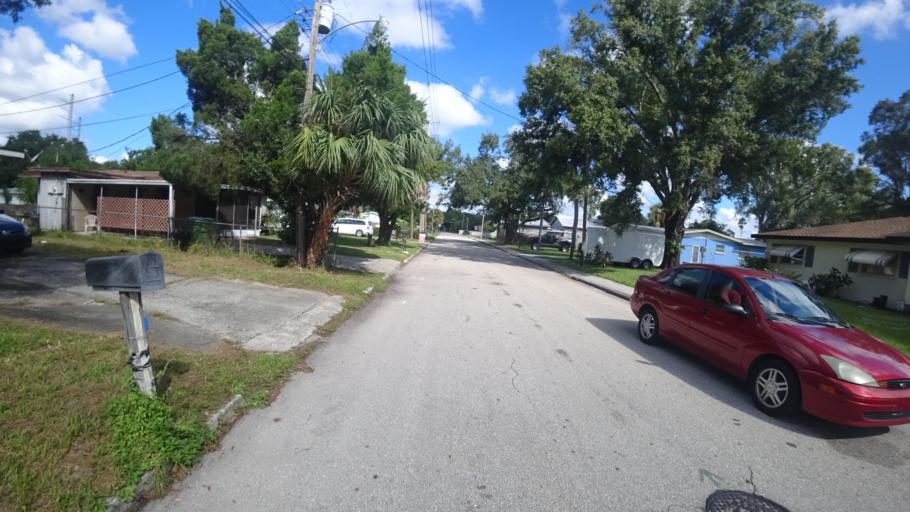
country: US
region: Florida
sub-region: Manatee County
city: Samoset
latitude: 27.4906
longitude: -82.5485
